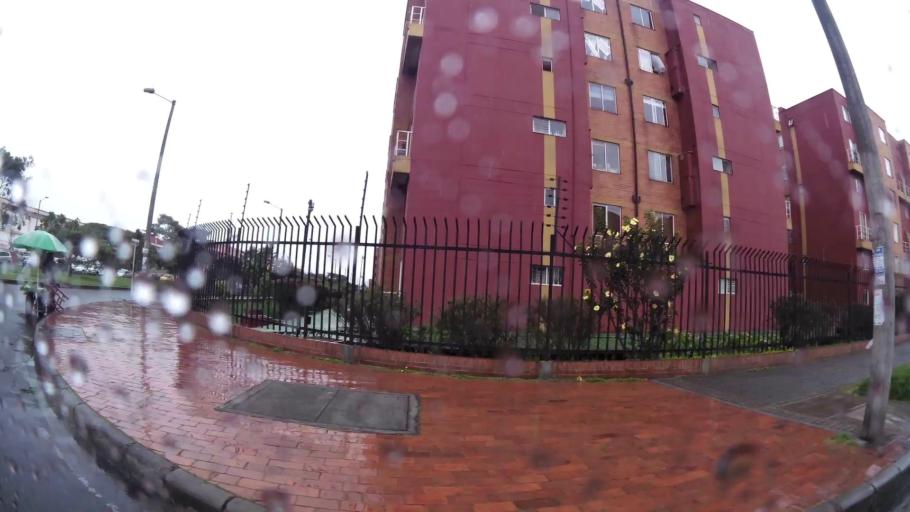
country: CO
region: Bogota D.C.
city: Bogota
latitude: 4.6607
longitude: -74.1315
